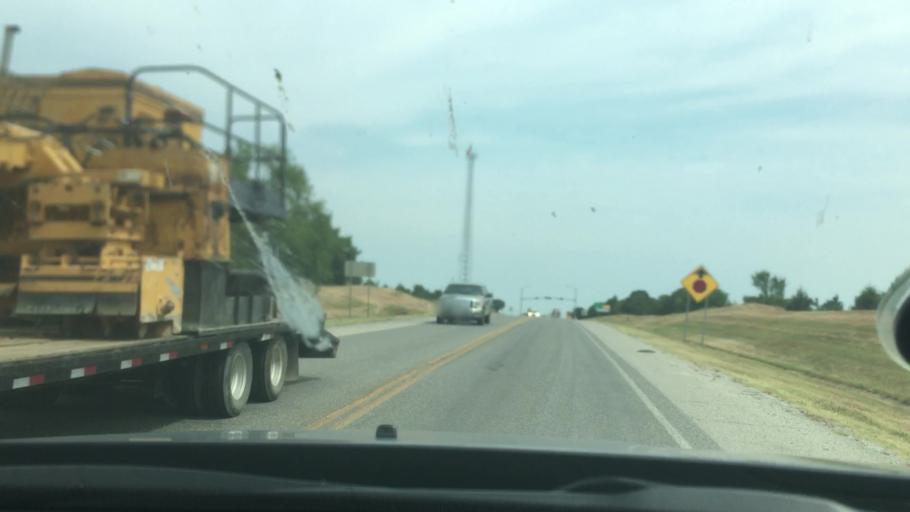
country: US
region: Oklahoma
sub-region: Coal County
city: Coalgate
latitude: 34.6087
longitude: -96.4244
